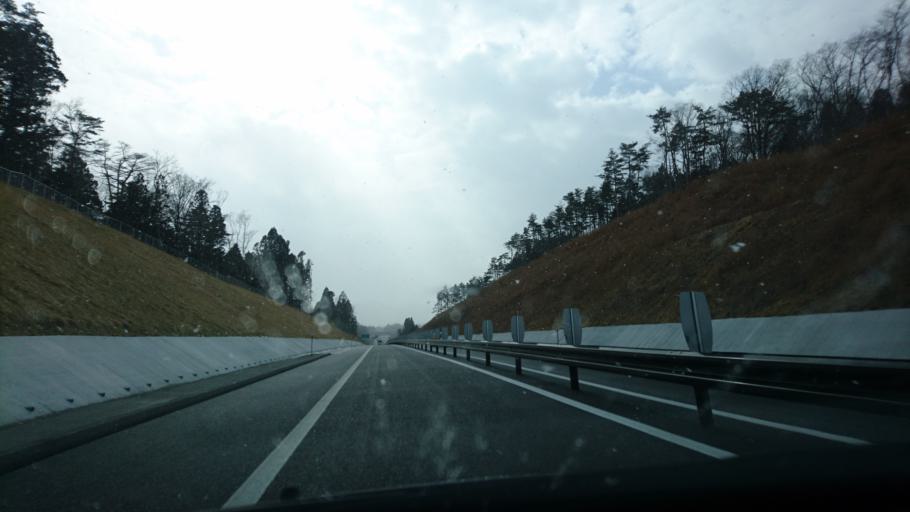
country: JP
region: Iwate
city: Ofunato
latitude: 38.7979
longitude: 141.5290
